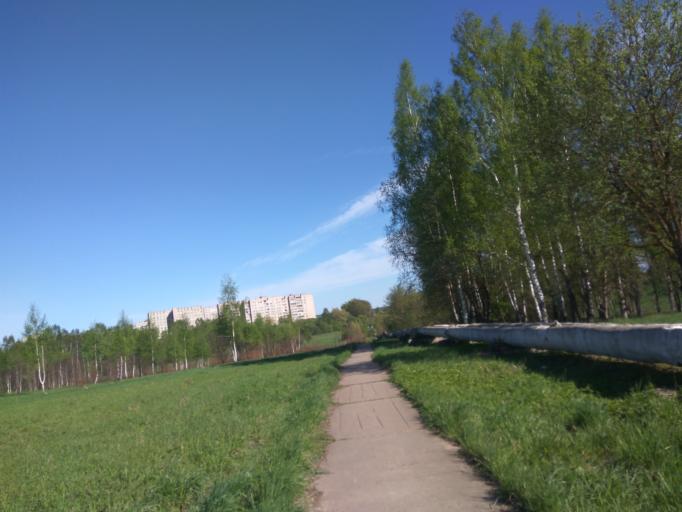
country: RU
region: Moskovskaya
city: Istra
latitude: 55.9075
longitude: 36.8458
